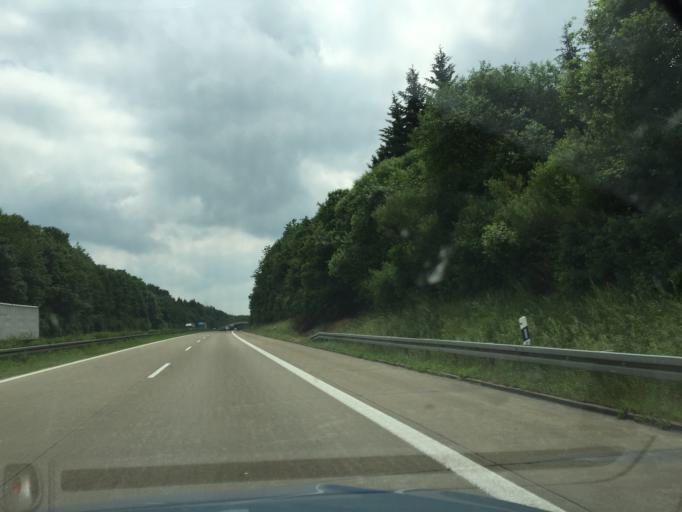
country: DE
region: Baden-Wuerttemberg
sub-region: Regierungsbezirk Stuttgart
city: Nattheim
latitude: 48.7775
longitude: 10.2118
